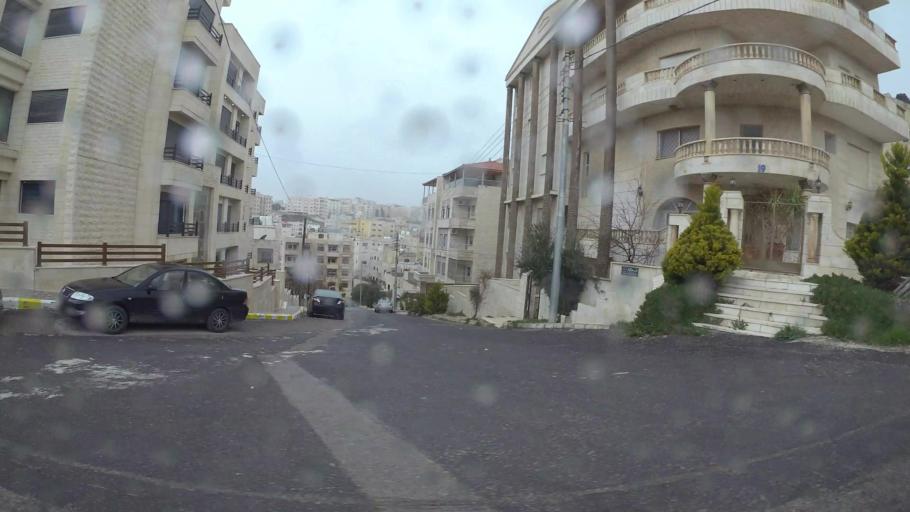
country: JO
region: Amman
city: Al Jubayhah
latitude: 31.9916
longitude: 35.8631
